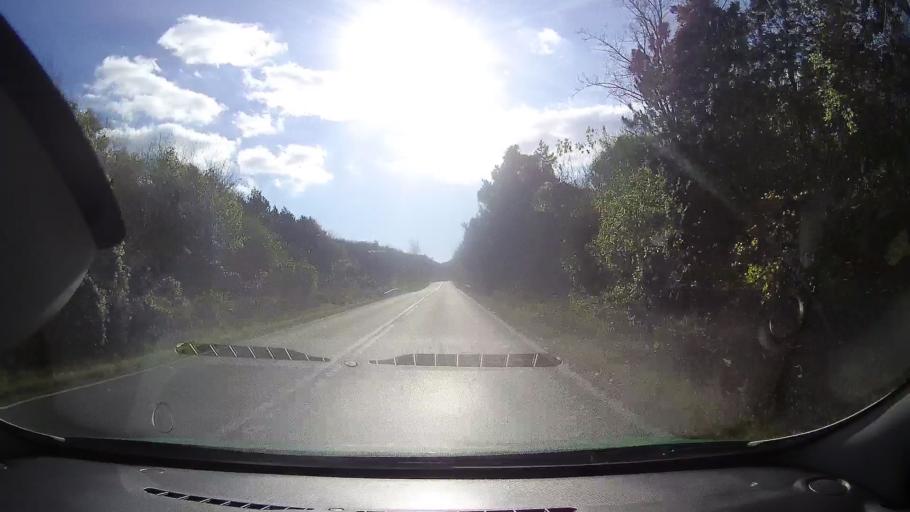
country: RO
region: Tulcea
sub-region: Oras Babadag
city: Babadag
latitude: 44.8694
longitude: 28.6885
